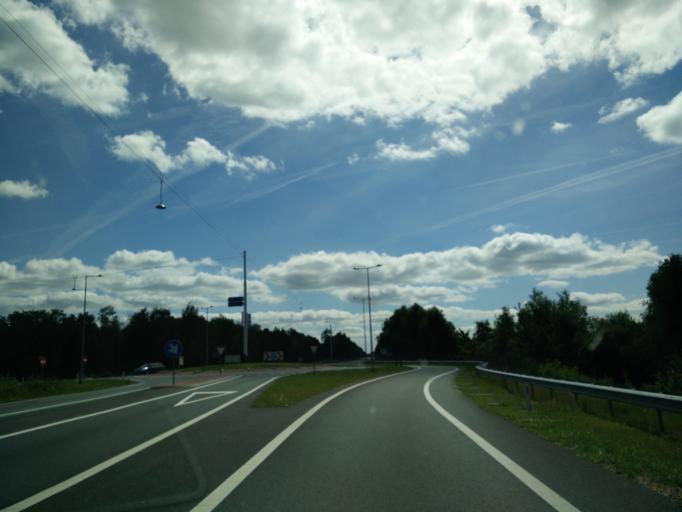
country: NL
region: Drenthe
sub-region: Gemeente Assen
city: Assen
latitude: 52.8771
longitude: 6.5147
